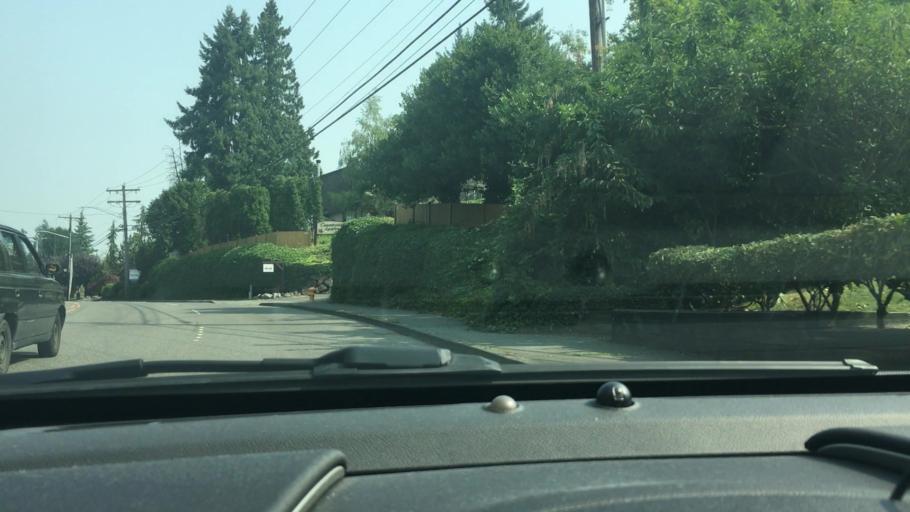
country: US
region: Washington
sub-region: Snohomish County
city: Alderwood Manor
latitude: 47.8229
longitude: -122.2818
